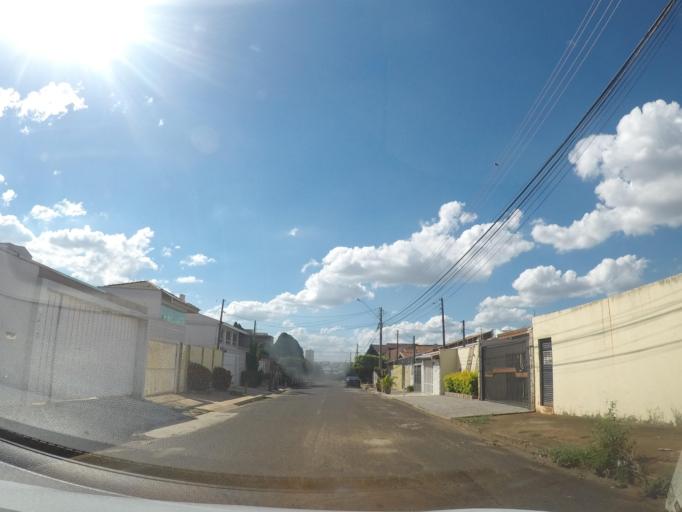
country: BR
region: Sao Paulo
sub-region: Sumare
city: Sumare
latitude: -22.8301
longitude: -47.2790
